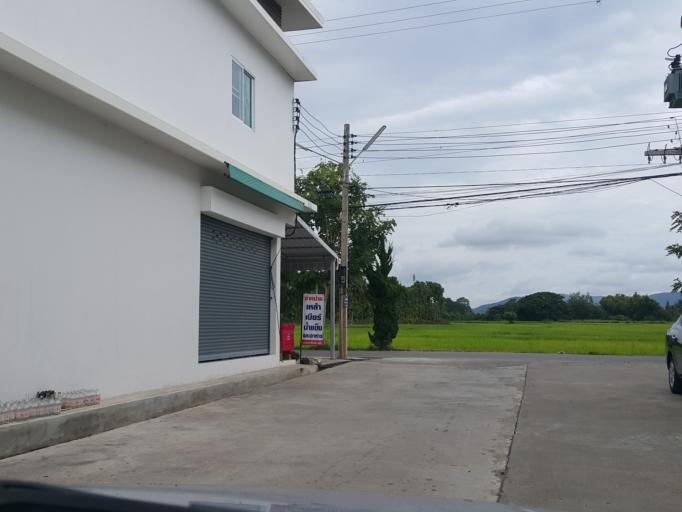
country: TH
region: Chiang Mai
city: San Sai
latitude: 18.8650
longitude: 99.1330
